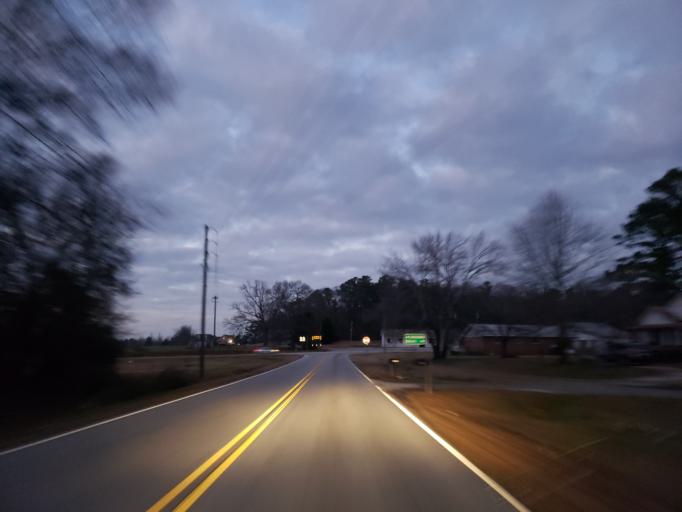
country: US
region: Georgia
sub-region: Carroll County
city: Temple
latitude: 33.8271
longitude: -85.0447
